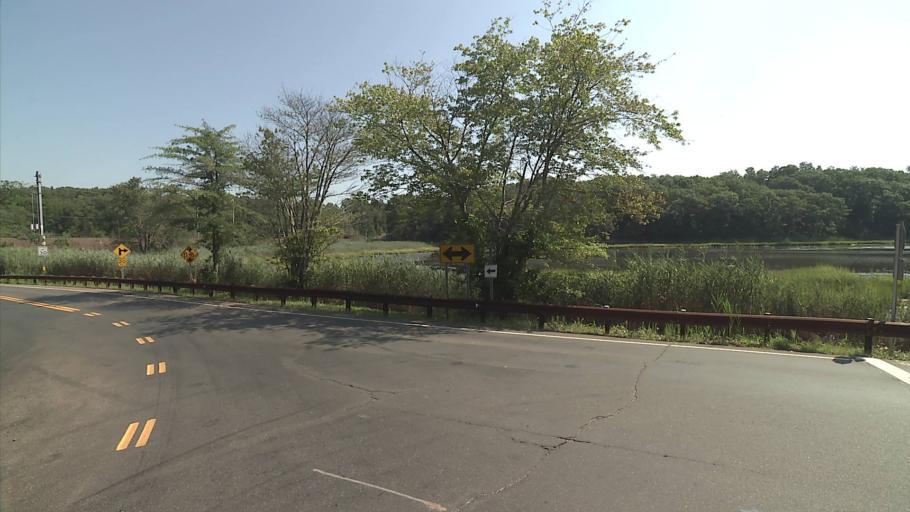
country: US
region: Connecticut
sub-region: New Haven County
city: Guilford Center
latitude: 41.2684
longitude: -72.6954
